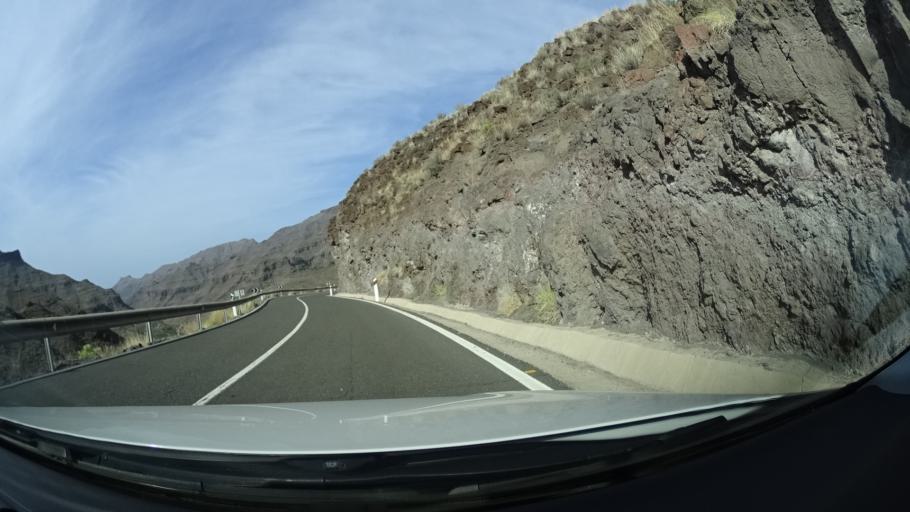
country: ES
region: Canary Islands
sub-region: Provincia de Las Palmas
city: Mogan
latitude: 27.9017
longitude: -15.7228
